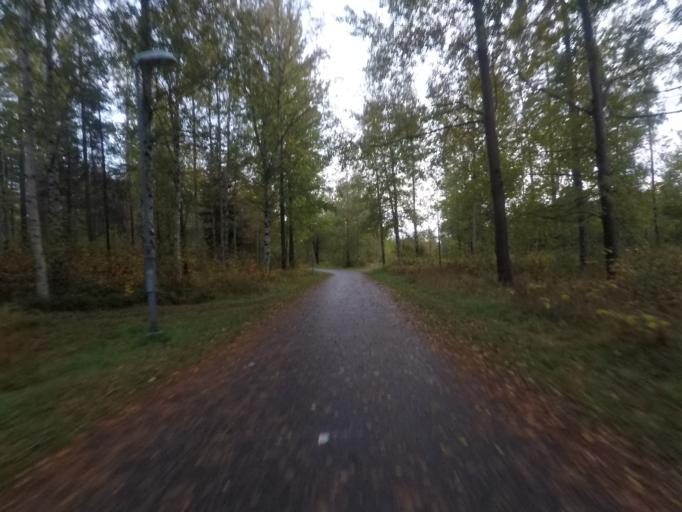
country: SE
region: OErebro
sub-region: Karlskoga Kommun
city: Karlskoga
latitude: 59.3145
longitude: 14.4865
